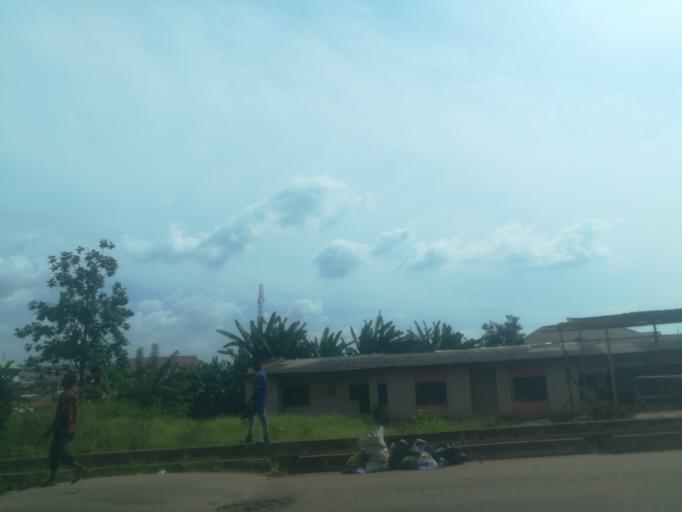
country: NG
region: Ogun
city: Abeokuta
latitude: 7.1625
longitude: 3.3754
